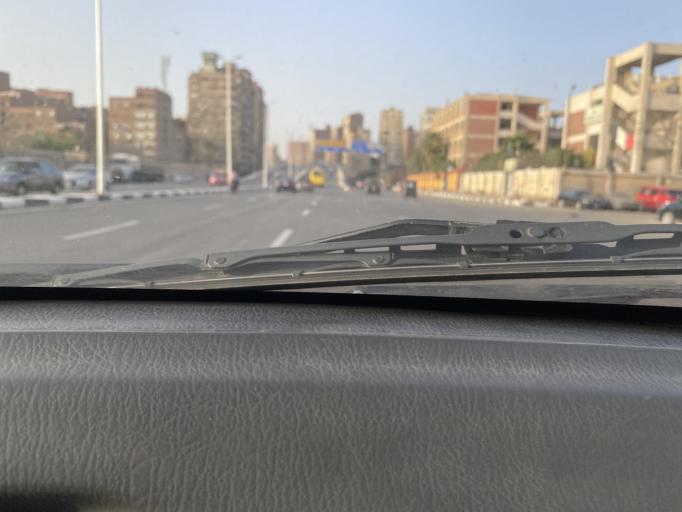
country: EG
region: Muhafazat al Qahirah
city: Cairo
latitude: 30.1167
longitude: 31.2966
